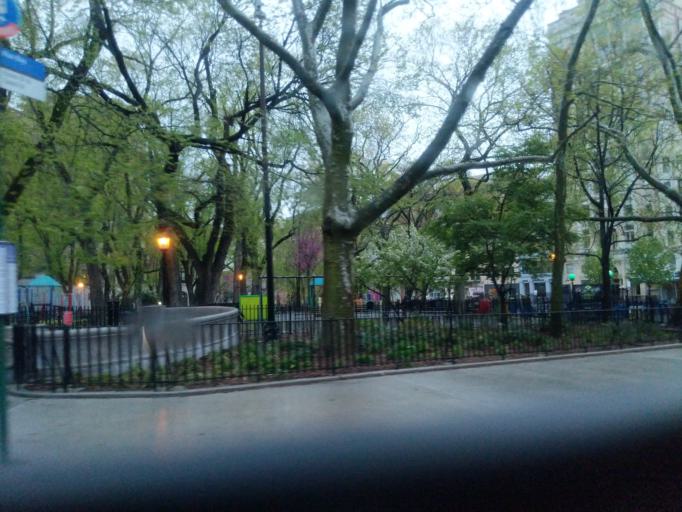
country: US
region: New York
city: New York City
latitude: 40.7146
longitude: -73.9902
